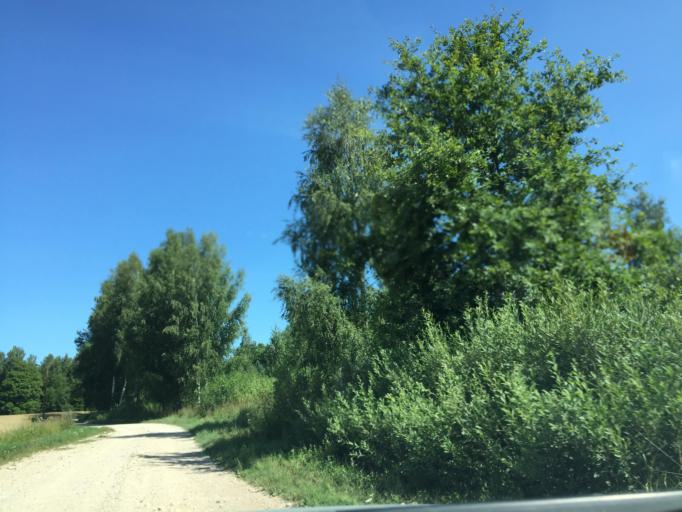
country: LV
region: Talsu Rajons
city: Stende
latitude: 57.1631
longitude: 22.2969
